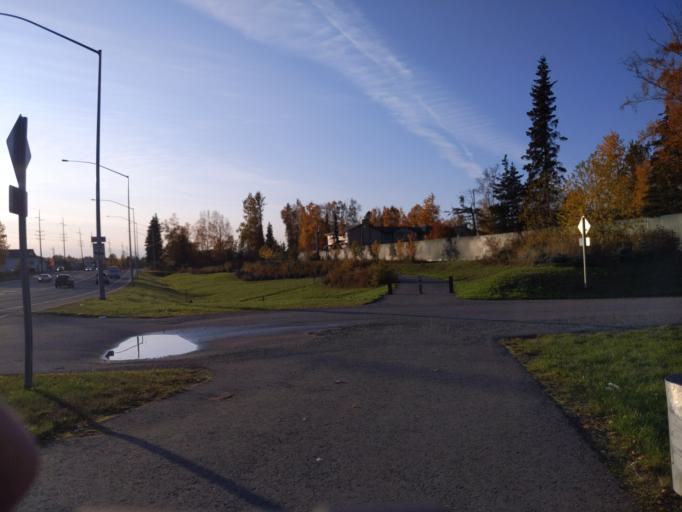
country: US
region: Alaska
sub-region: Anchorage Municipality
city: Anchorage
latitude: 61.1666
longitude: -149.8752
